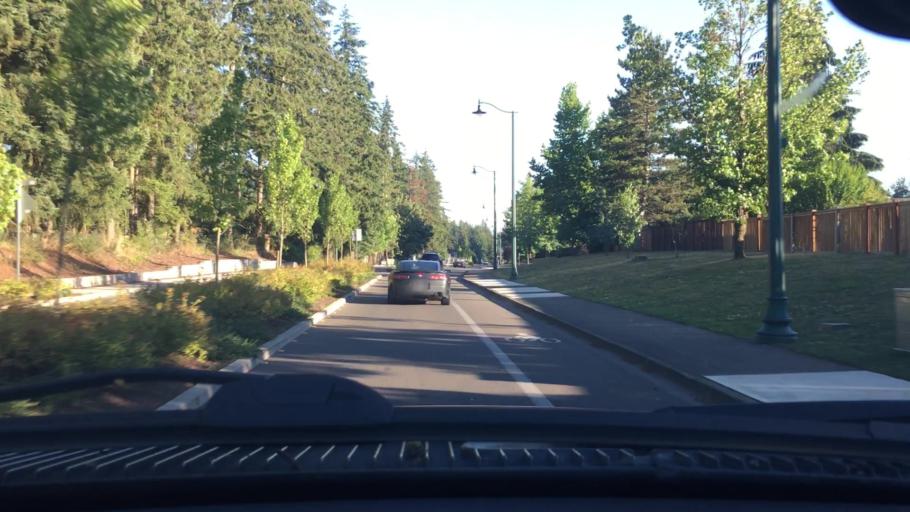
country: US
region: Washington
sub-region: King County
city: Maple Valley
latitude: 47.3535
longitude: -122.0536
